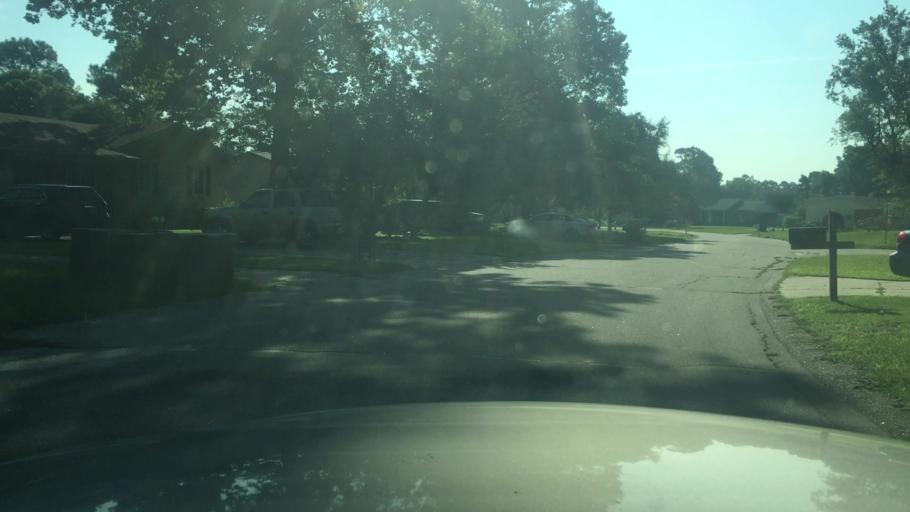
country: US
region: North Carolina
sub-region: Cumberland County
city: Spring Lake
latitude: 35.1588
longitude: -78.9085
